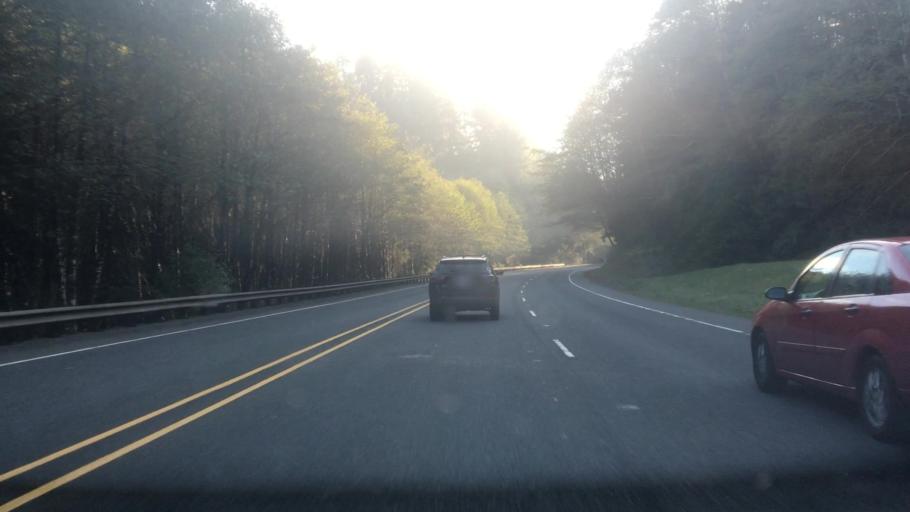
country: US
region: Oregon
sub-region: Clatsop County
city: Cannon Beach
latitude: 45.9231
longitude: -123.9327
